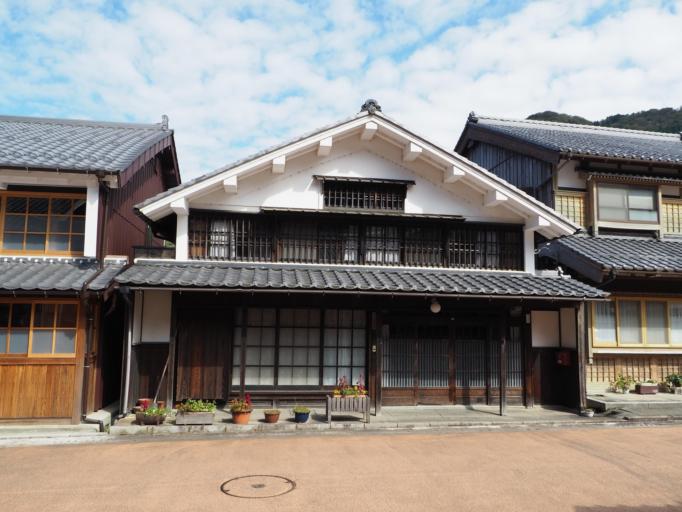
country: JP
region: Fukui
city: Obama
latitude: 35.4438
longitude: 135.9004
